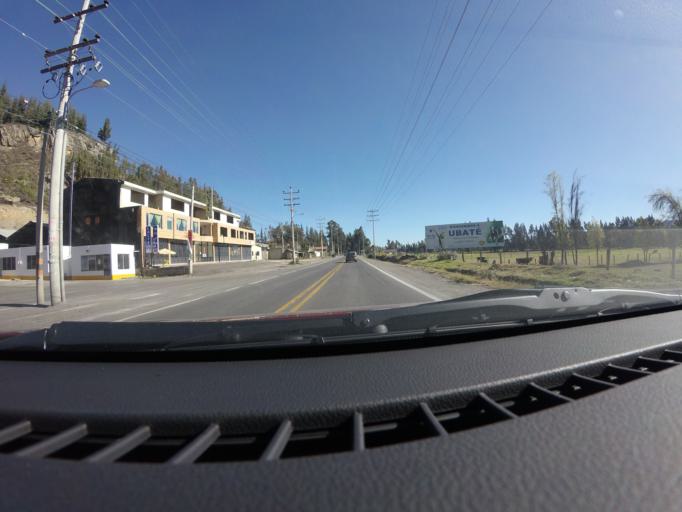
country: CO
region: Cundinamarca
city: Ubate
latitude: 5.2929
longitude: -73.8159
